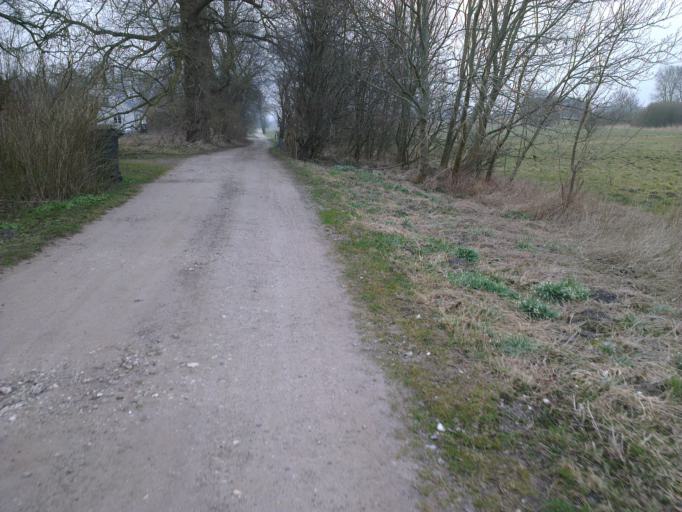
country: DK
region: Capital Region
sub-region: Frederikssund Kommune
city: Frederikssund
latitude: 55.7717
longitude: 12.0354
